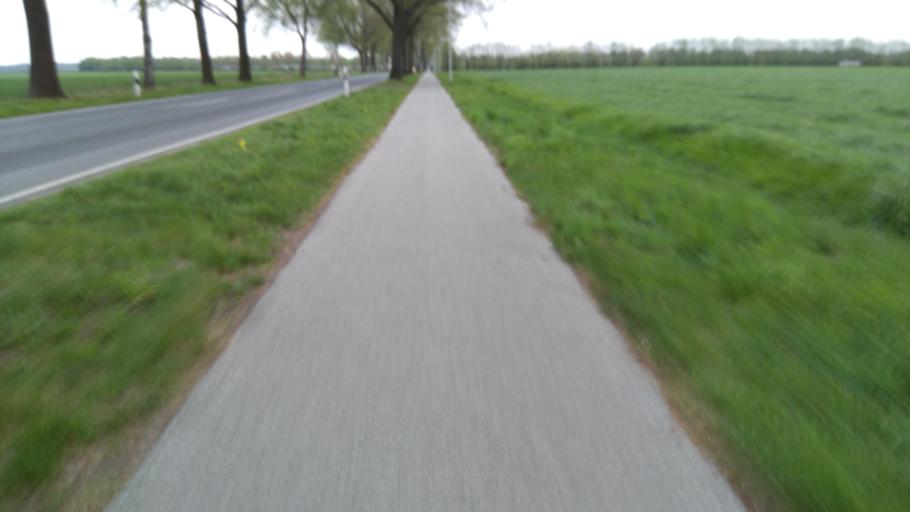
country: DE
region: Lower Saxony
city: Apensen
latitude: 53.4455
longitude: 9.6355
